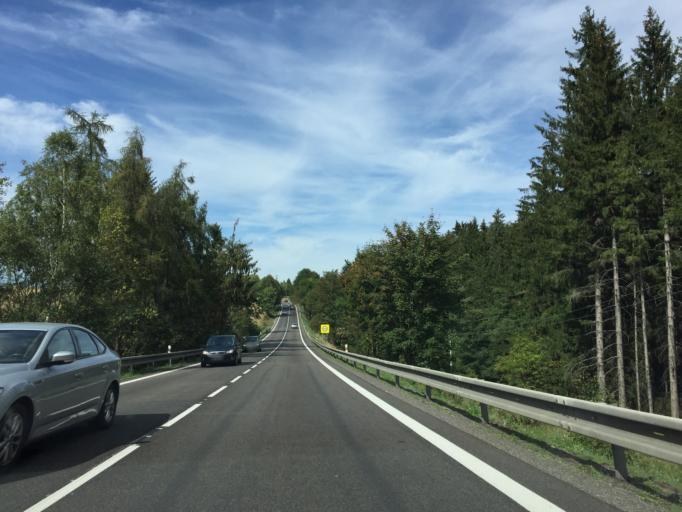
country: CZ
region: Central Bohemia
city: Votice
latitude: 49.5940
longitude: 14.6616
